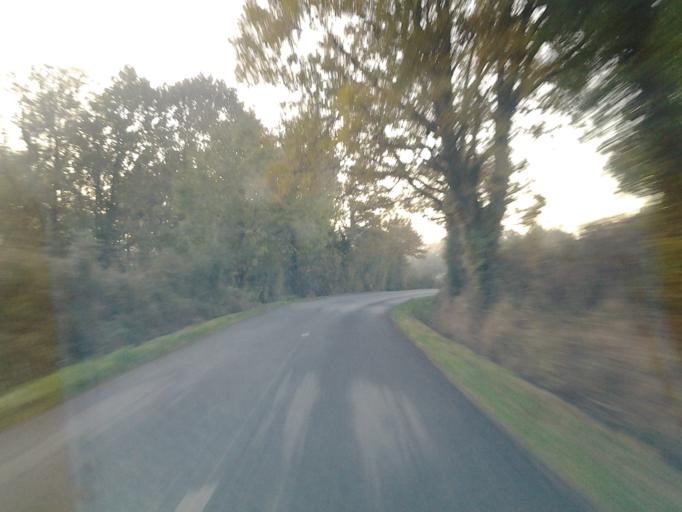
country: FR
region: Pays de la Loire
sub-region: Departement de la Vendee
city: Chateau-Guibert
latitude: 46.6299
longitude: -1.2331
